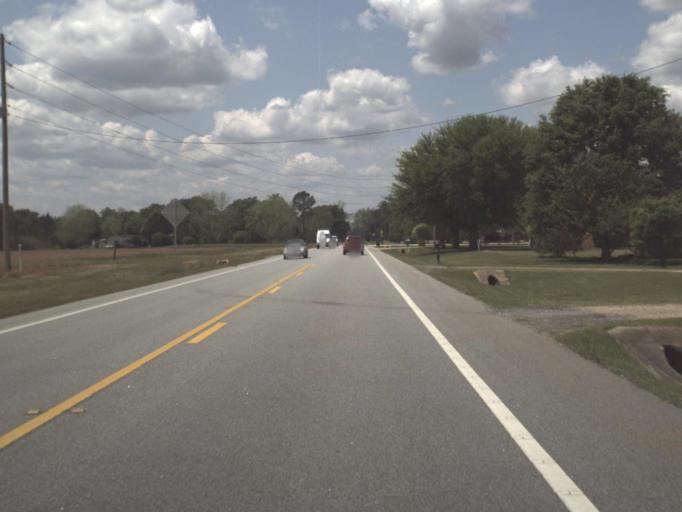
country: US
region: Alabama
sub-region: Escambia County
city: Atmore
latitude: 30.8861
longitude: -87.4538
